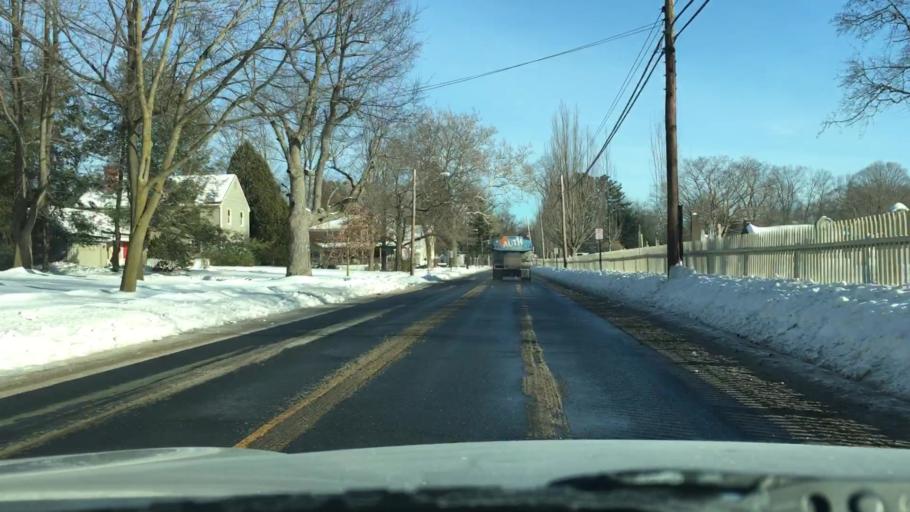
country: US
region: Massachusetts
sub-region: Hampden County
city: Longmeadow
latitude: 42.0502
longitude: -72.5793
